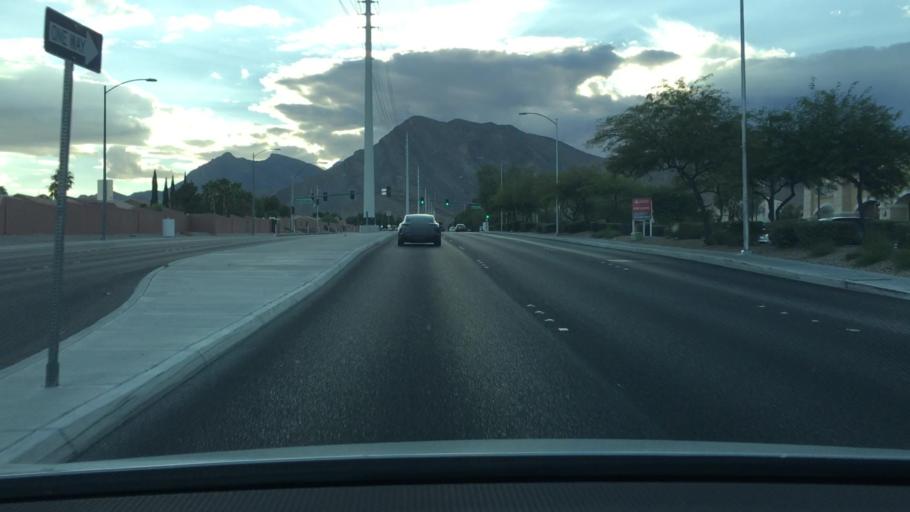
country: US
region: Nevada
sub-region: Clark County
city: Summerlin South
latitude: 36.2184
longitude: -115.3140
